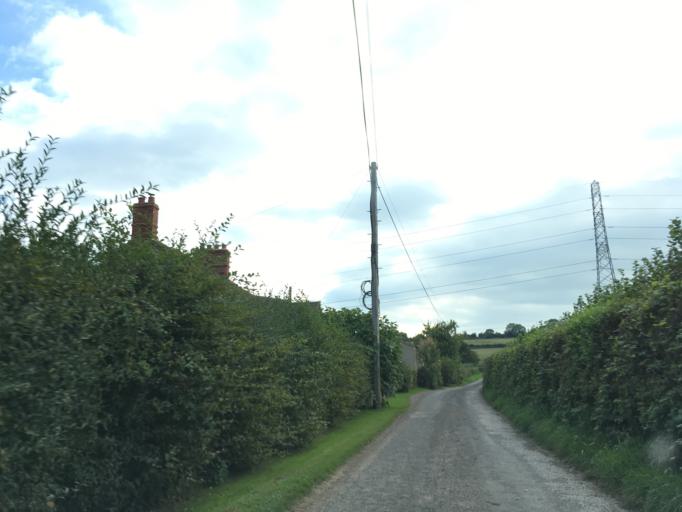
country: GB
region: England
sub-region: South Gloucestershire
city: Tytherington
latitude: 51.6141
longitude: -2.4699
